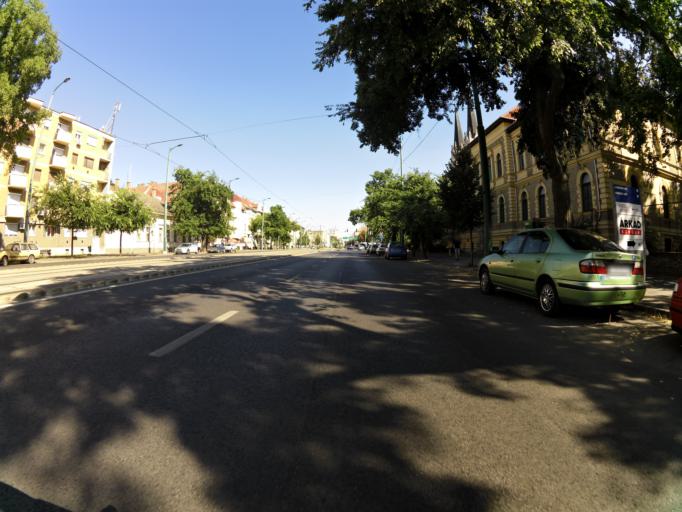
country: HU
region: Csongrad
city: Szeged
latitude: 46.2603
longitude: 20.1397
